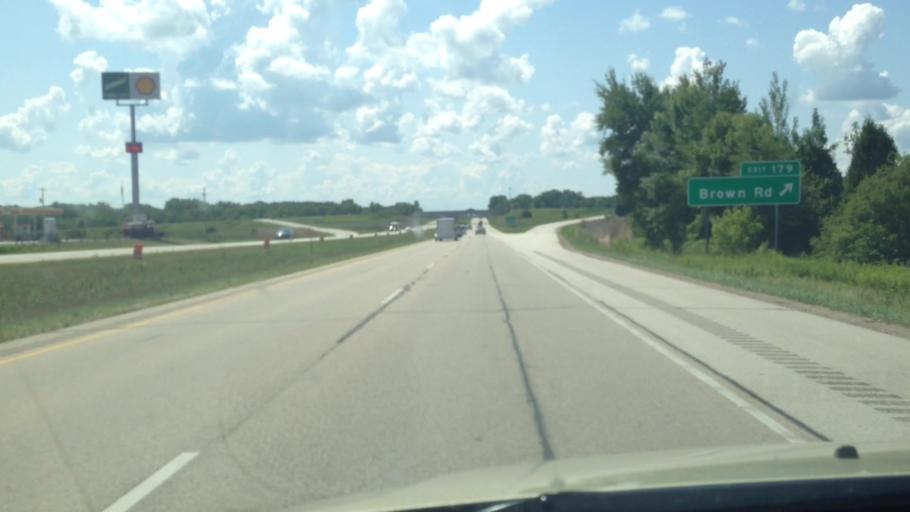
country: US
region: Wisconsin
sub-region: Brown County
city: Suamico
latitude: 44.6828
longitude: -88.0509
